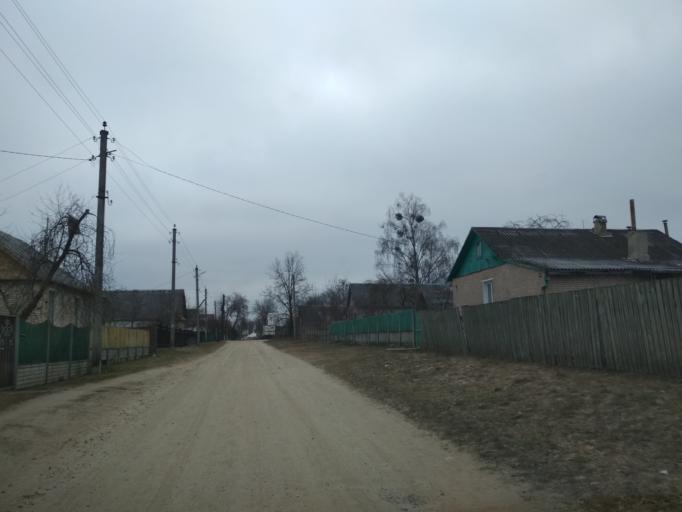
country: BY
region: Minsk
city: Mar''ina Horka
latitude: 53.5144
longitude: 28.1505
